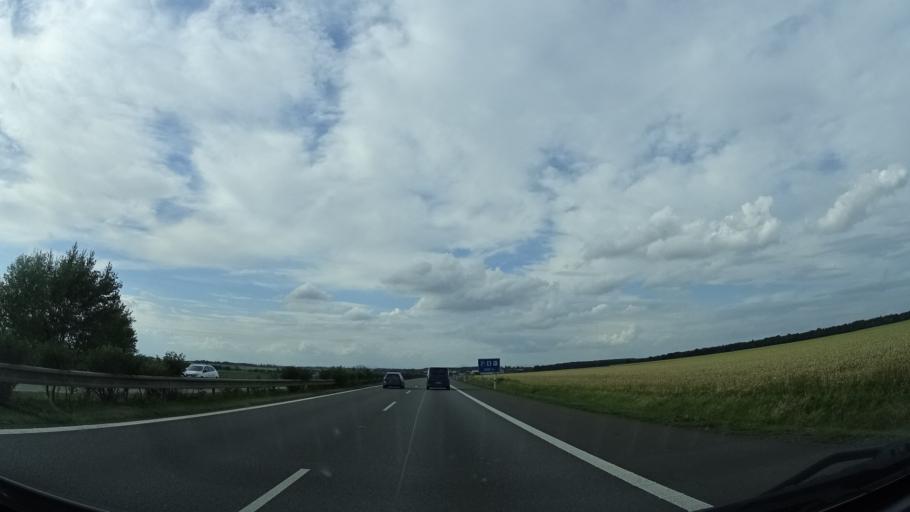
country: CZ
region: Central Bohemia
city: Zdiby
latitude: 50.1848
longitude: 14.4461
